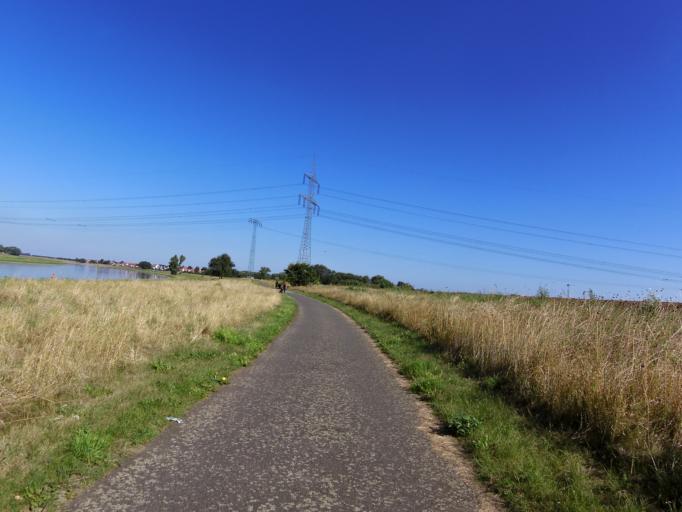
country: DE
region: Saxony
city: Riesa
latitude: 51.3355
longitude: 13.2943
